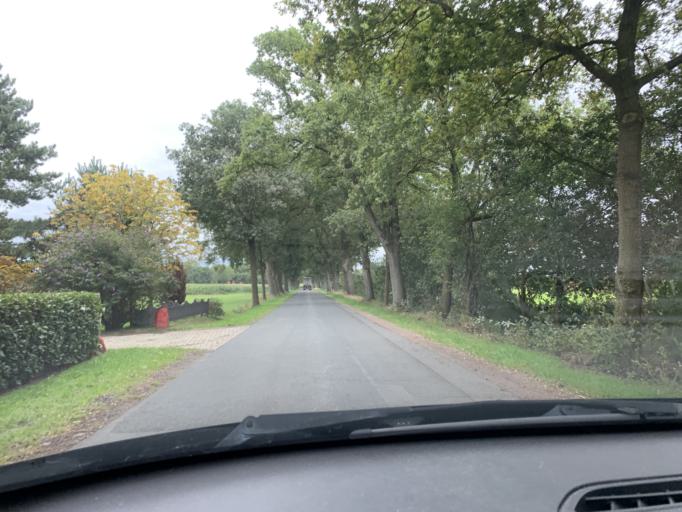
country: DE
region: Lower Saxony
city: Westerstede
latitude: 53.2777
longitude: 7.8873
